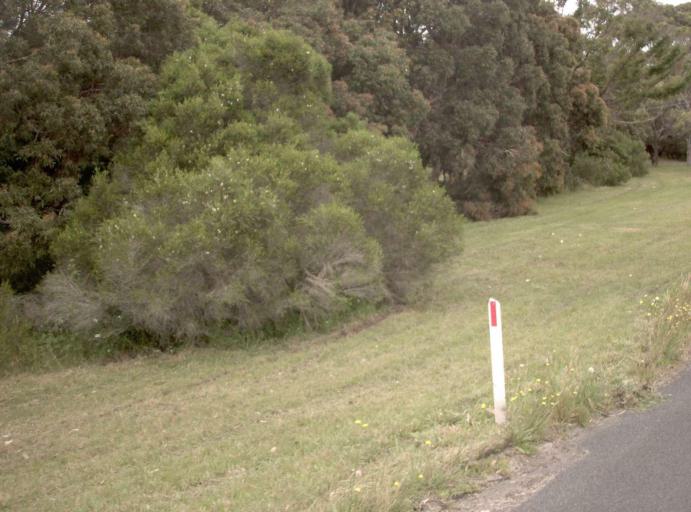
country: AU
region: Victoria
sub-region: Mornington Peninsula
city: Mount Martha
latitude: -38.2936
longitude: 145.0290
